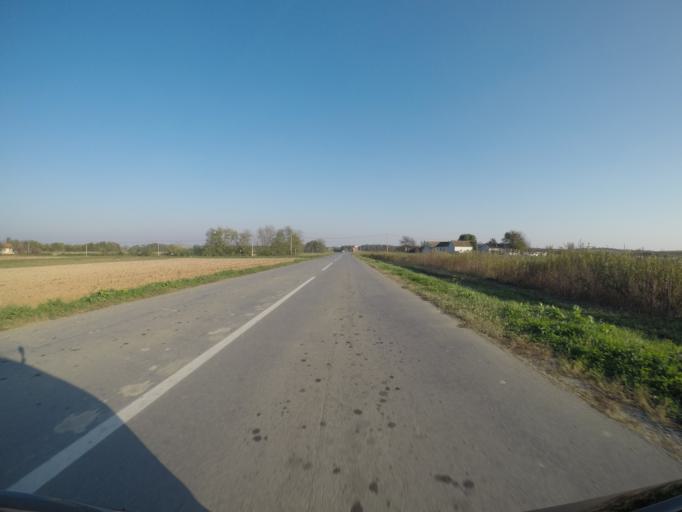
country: HR
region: Virovitick-Podravska
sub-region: Grad Virovitica
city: Virovitica
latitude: 45.8837
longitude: 17.3869
